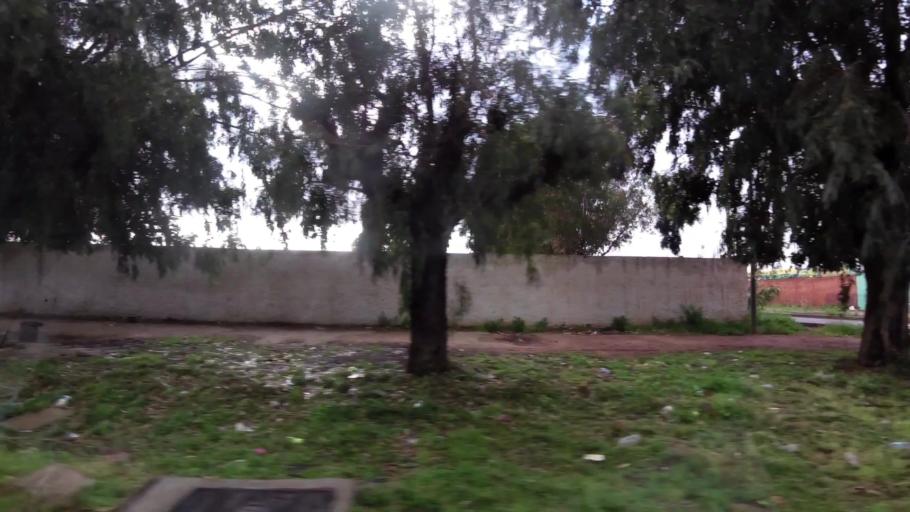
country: MA
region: Grand Casablanca
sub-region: Casablanca
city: Casablanca
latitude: 33.5598
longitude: -7.6510
